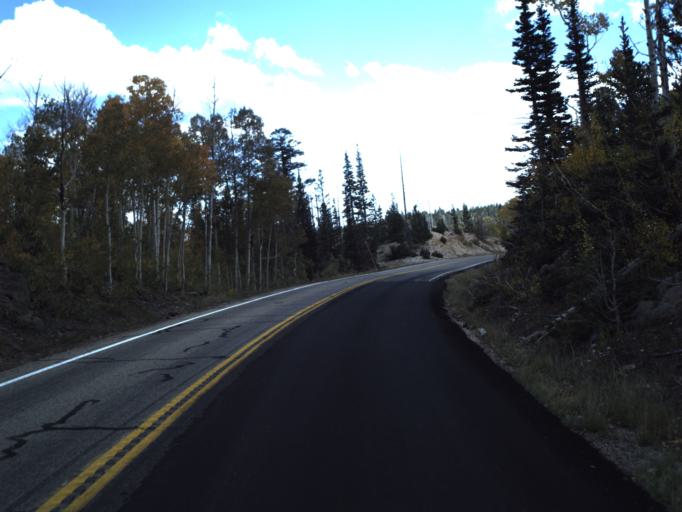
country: US
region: Utah
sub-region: Iron County
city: Parowan
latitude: 37.5394
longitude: -112.7759
